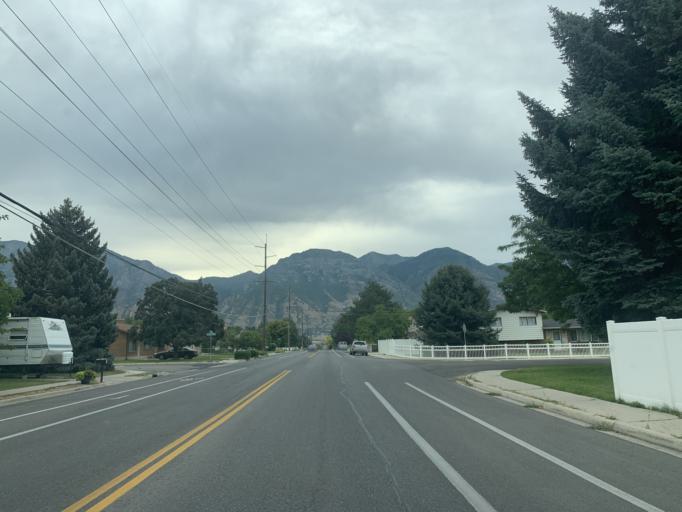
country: US
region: Utah
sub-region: Utah County
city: Provo
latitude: 40.2534
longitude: -111.6838
